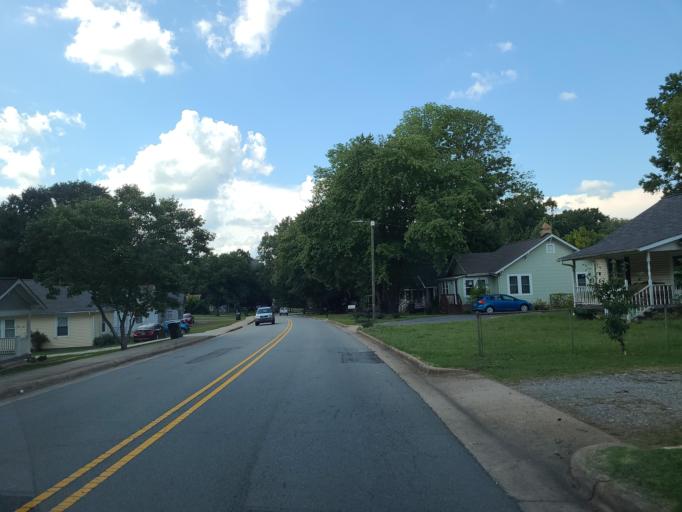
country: US
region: North Carolina
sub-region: Gaston County
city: Lowell
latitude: 35.2789
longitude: -81.0986
